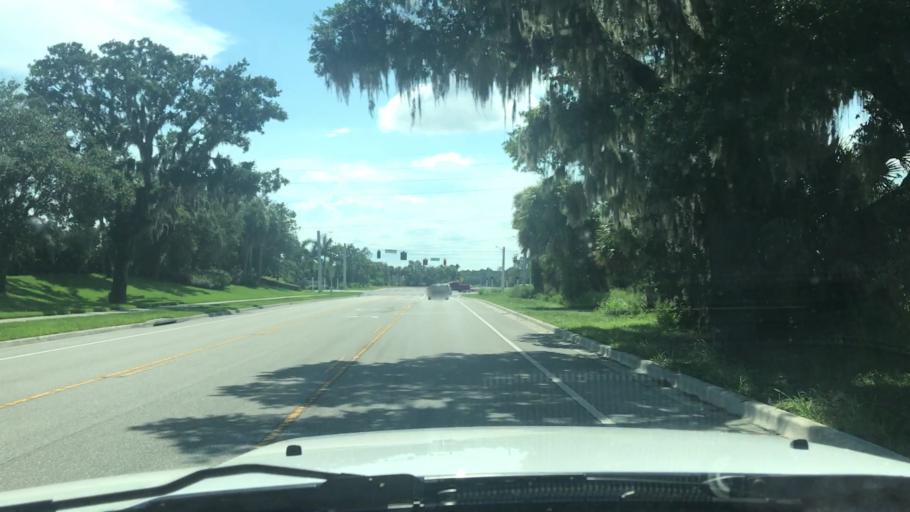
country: US
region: Florida
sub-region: Indian River County
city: Florida Ridge
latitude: 27.5723
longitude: -80.4128
